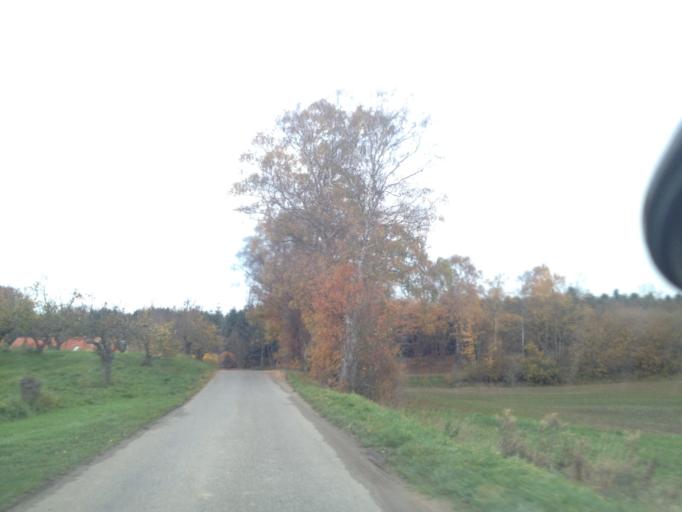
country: DK
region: South Denmark
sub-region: Assens Kommune
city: Vissenbjerg
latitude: 55.4197
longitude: 10.1607
